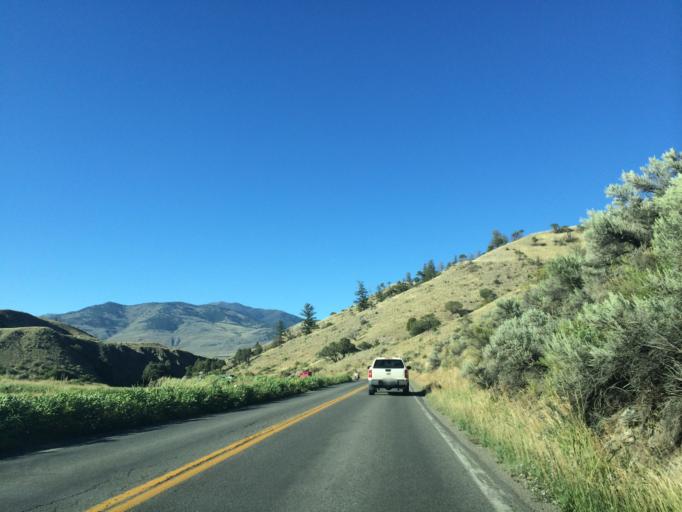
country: US
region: Montana
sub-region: Gallatin County
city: West Yellowstone
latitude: 44.9966
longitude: -110.6931
